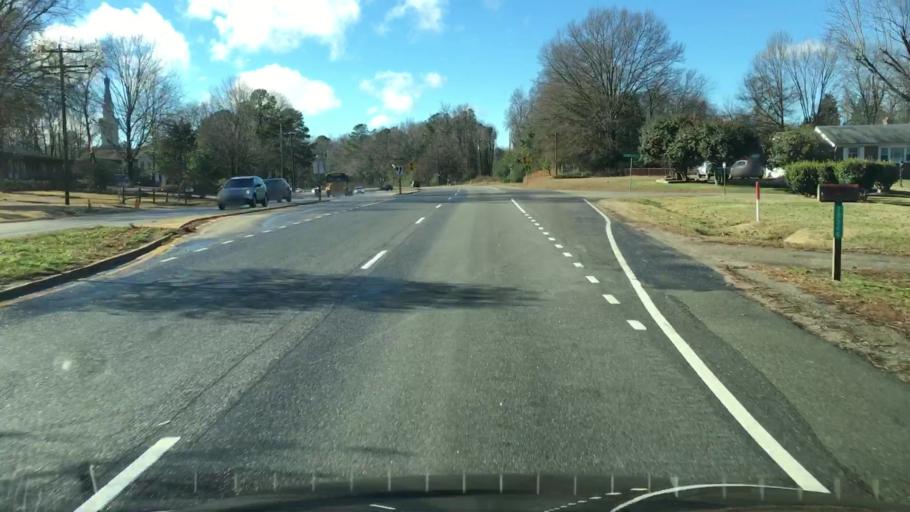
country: US
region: Virginia
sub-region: Chesterfield County
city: Bon Air
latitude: 37.5333
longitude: -77.5875
